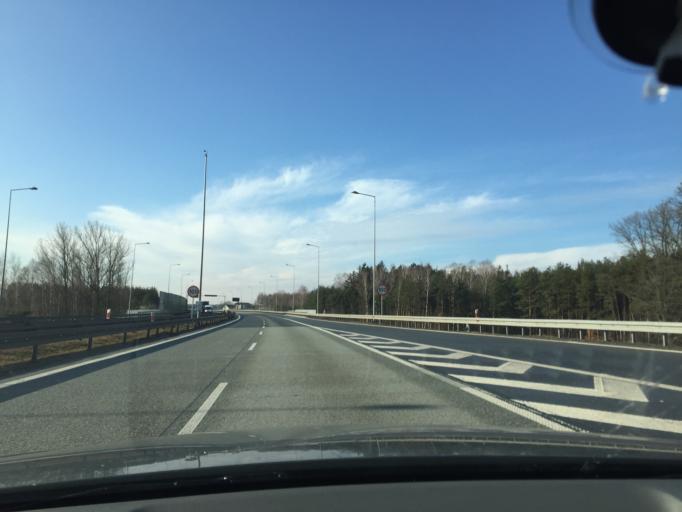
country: PL
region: Lodz Voivodeship
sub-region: Powiat tomaszowski
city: Czerniewice
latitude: 51.6546
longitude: 20.1498
